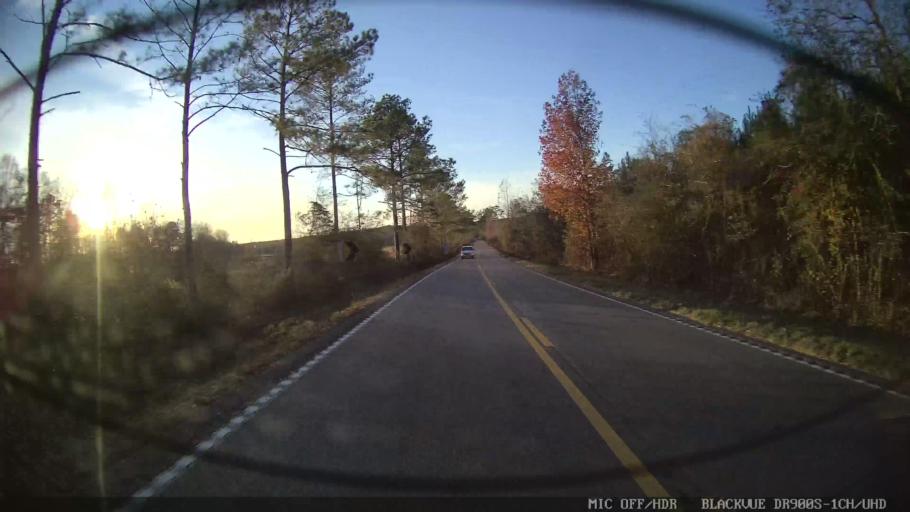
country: US
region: Mississippi
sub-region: Lamar County
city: Lumberton
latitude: 31.0001
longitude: -89.3456
